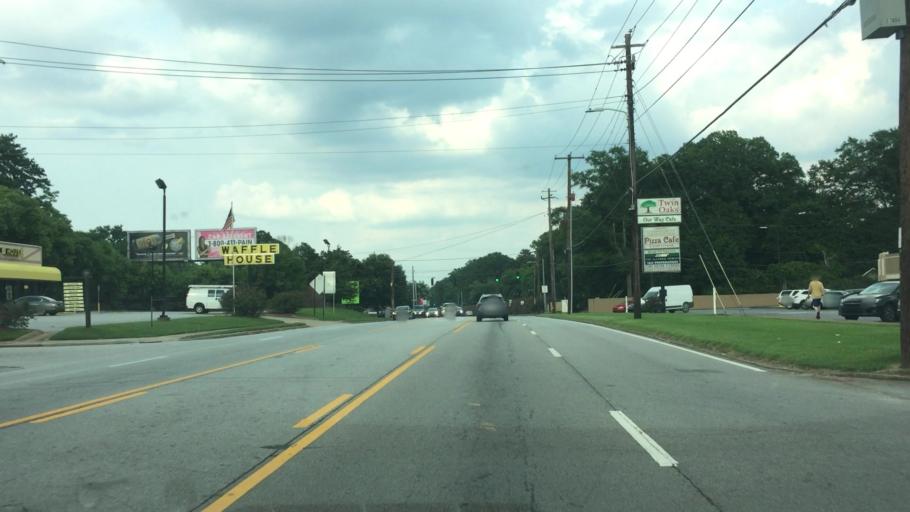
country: US
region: Georgia
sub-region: DeKalb County
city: Avondale Estates
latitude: 33.7751
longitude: -84.2744
